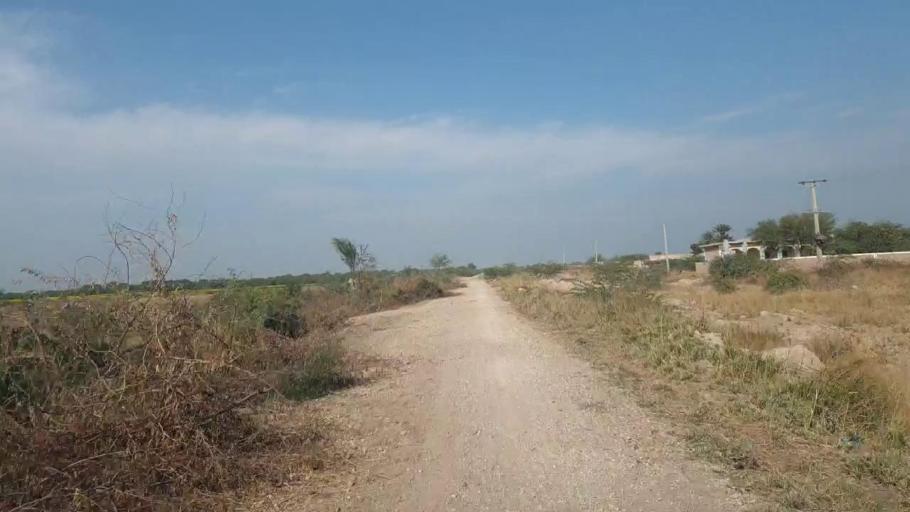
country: PK
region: Sindh
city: Shahdadpur
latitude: 25.9900
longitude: 68.5476
